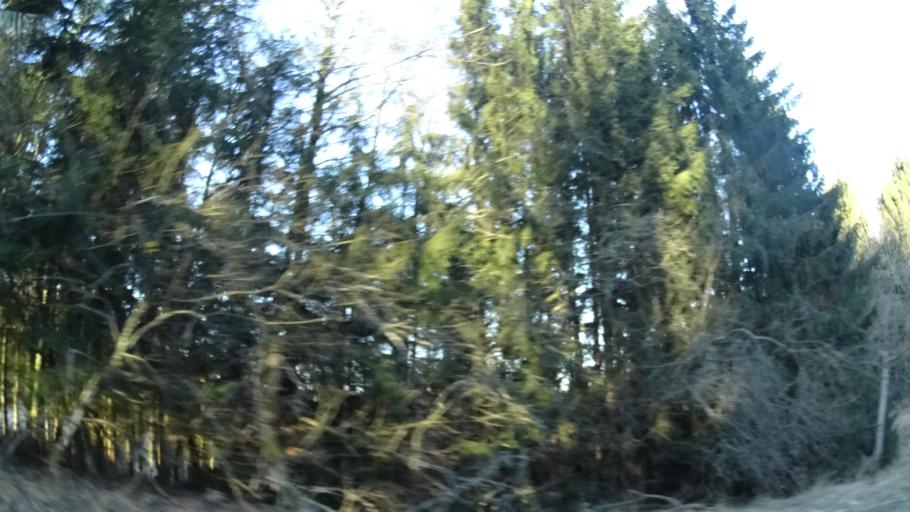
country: DE
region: Bavaria
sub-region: Upper Franconia
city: Tettau
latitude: 50.4492
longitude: 11.2462
